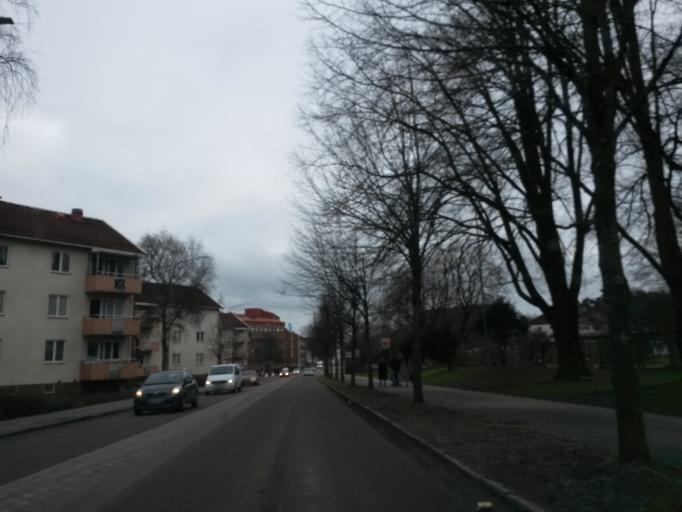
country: SE
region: Vaestra Goetaland
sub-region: Boras Kommun
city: Boras
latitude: 57.7251
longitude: 12.9239
